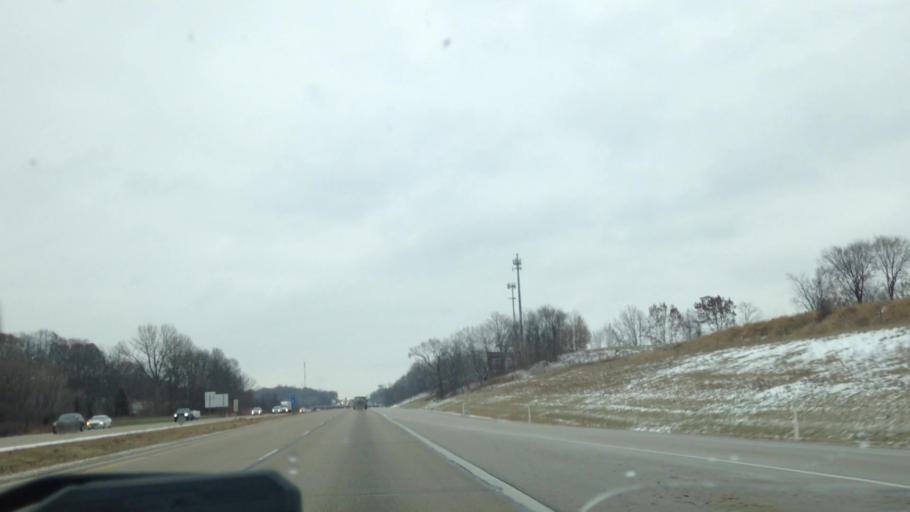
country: US
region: Wisconsin
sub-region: Washington County
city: Slinger
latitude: 43.3449
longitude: -88.2791
